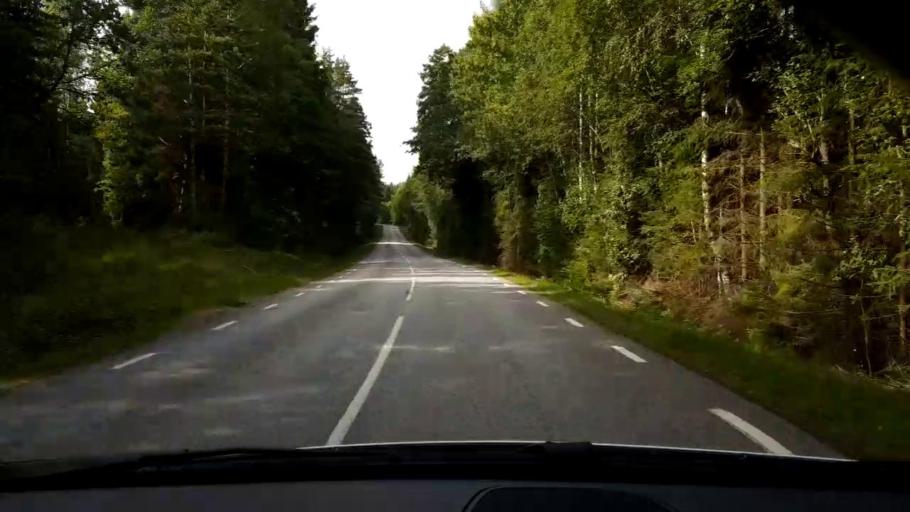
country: SE
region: Joenkoeping
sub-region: Vetlanda Kommun
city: Vetlanda
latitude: 57.3297
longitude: 15.0847
